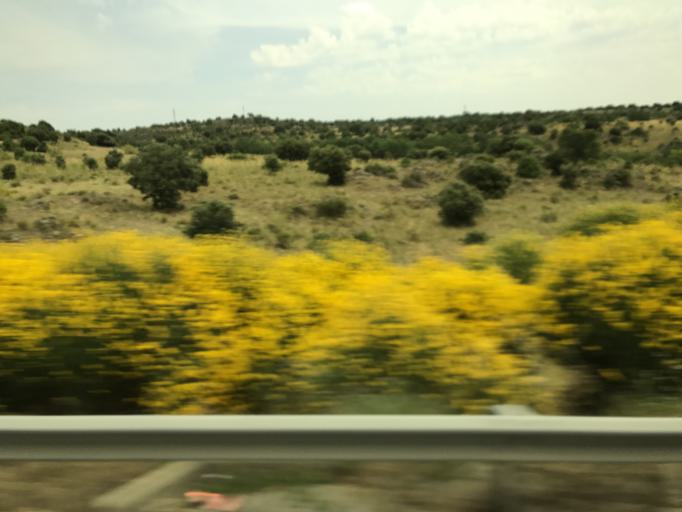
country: ES
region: Madrid
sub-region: Provincia de Madrid
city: Cabanillas de la Sierra
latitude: 40.8366
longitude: -3.6199
